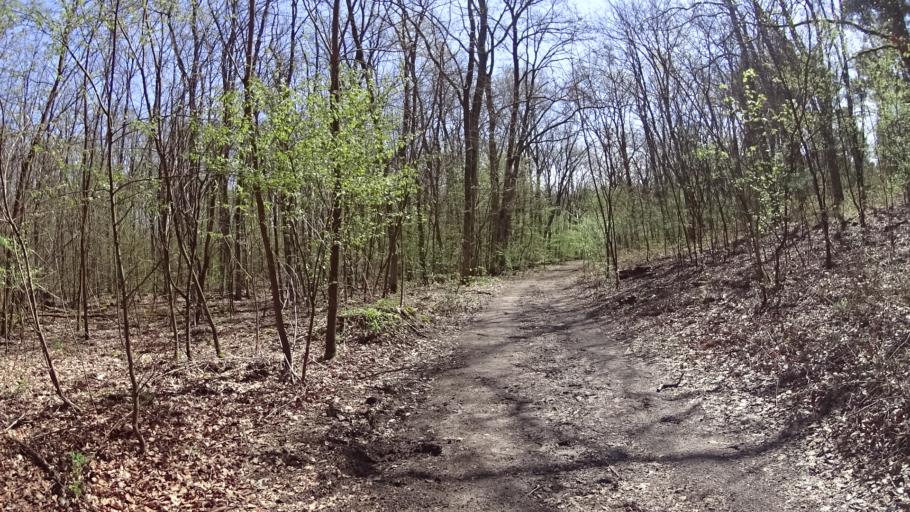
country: DE
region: Hesse
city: Viernheim
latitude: 49.5591
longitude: 8.5914
